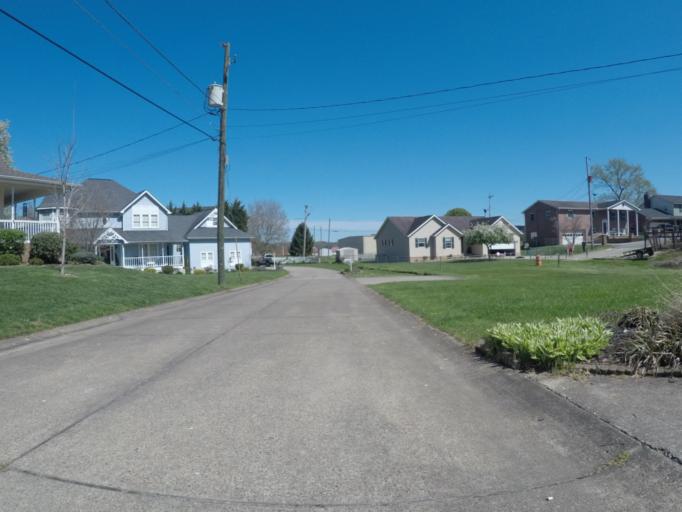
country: US
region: West Virginia
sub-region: Cabell County
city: Pea Ridge
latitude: 38.4154
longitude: -82.3075
